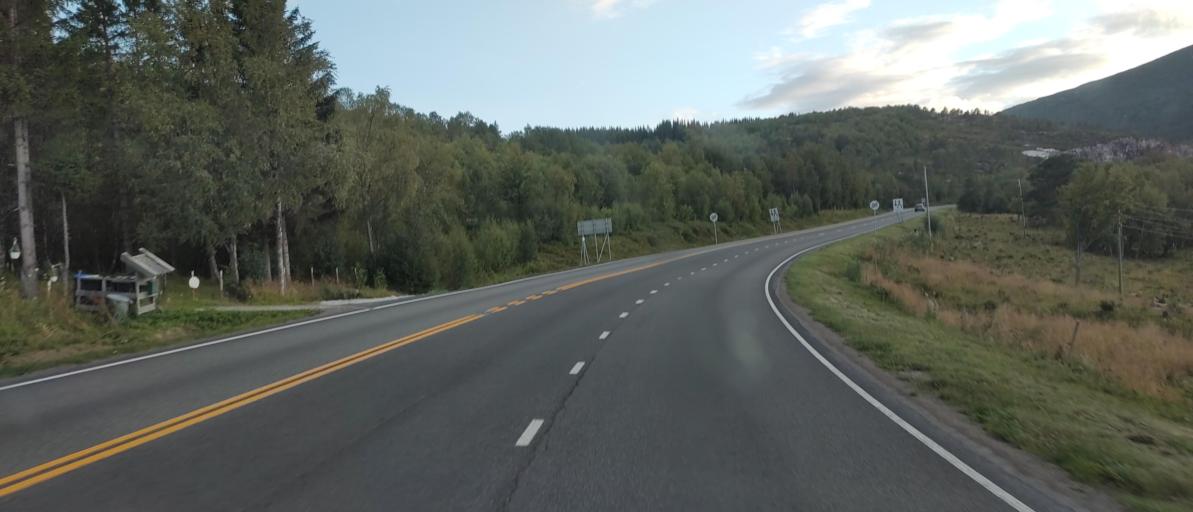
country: NO
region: Nordland
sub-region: Lodingen
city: Lodingen
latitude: 68.2194
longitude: 16.0696
